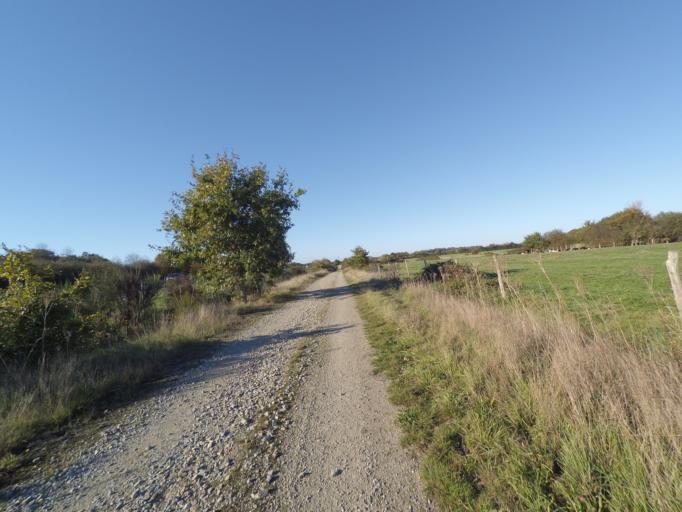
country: FR
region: Pays de la Loire
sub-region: Departement de la Loire-Atlantique
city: La Planche
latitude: 47.0230
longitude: -1.3989
